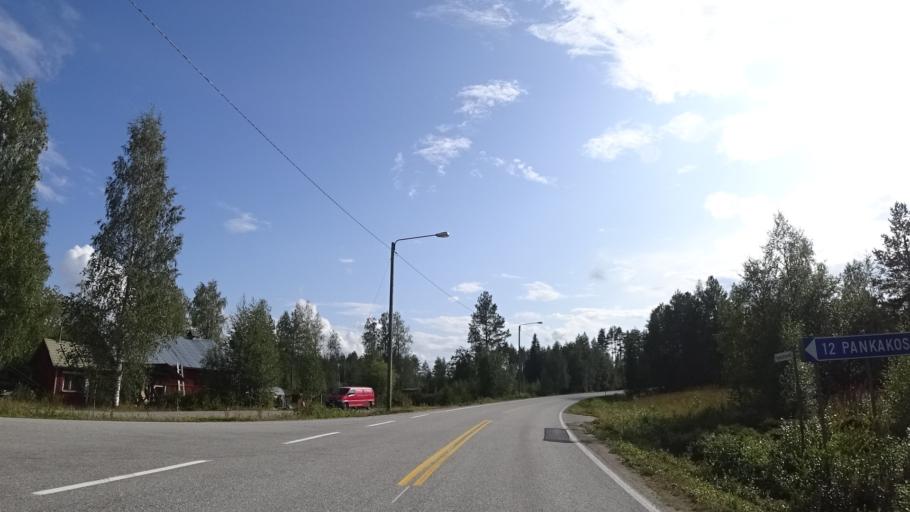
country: FI
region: North Karelia
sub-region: Pielisen Karjala
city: Lieksa
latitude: 63.4194
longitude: 30.1049
